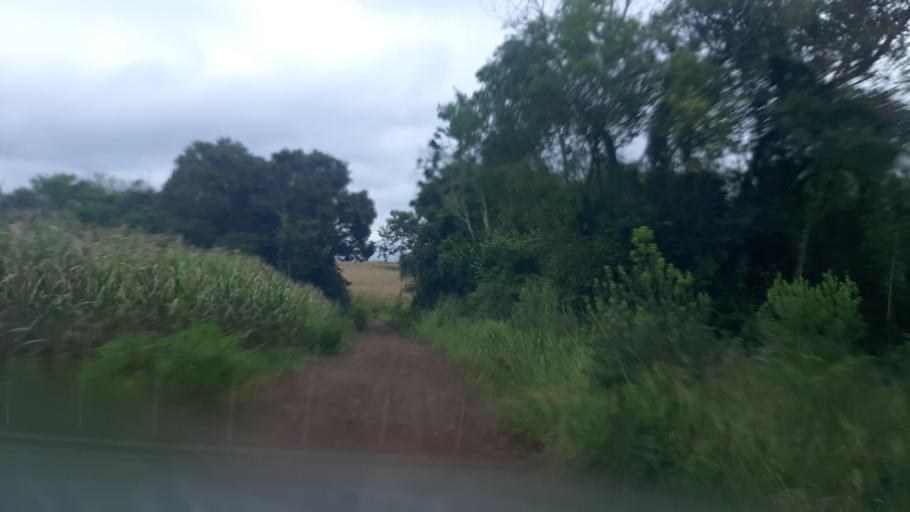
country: BR
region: Parana
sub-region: Ampere
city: Ampere
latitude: -26.0495
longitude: -53.5301
